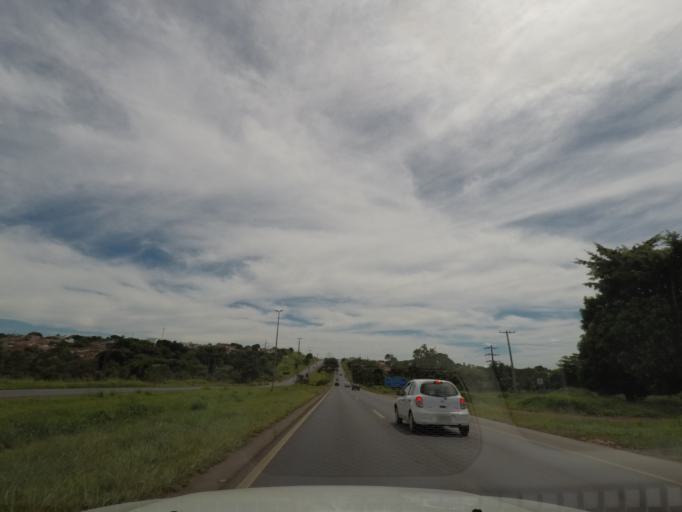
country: BR
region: Goias
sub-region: Planaltina
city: Planaltina
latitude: -15.6080
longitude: -47.6926
